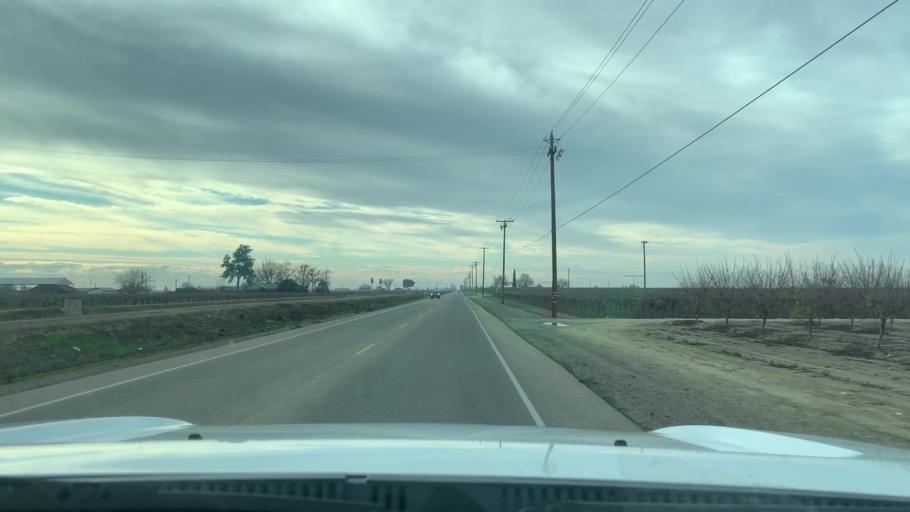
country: US
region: California
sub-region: Fresno County
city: Fowler
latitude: 36.6055
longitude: -119.7067
